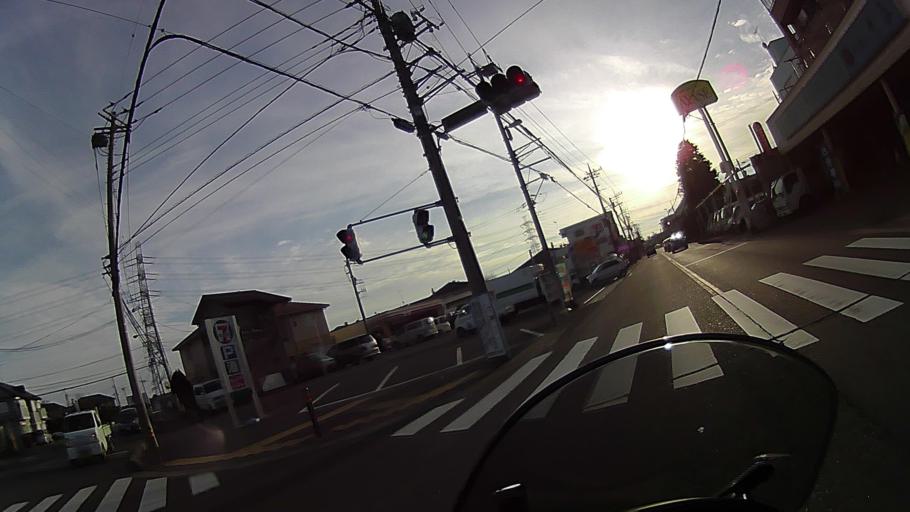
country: JP
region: Kanagawa
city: Minami-rinkan
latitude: 35.4250
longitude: 139.4289
